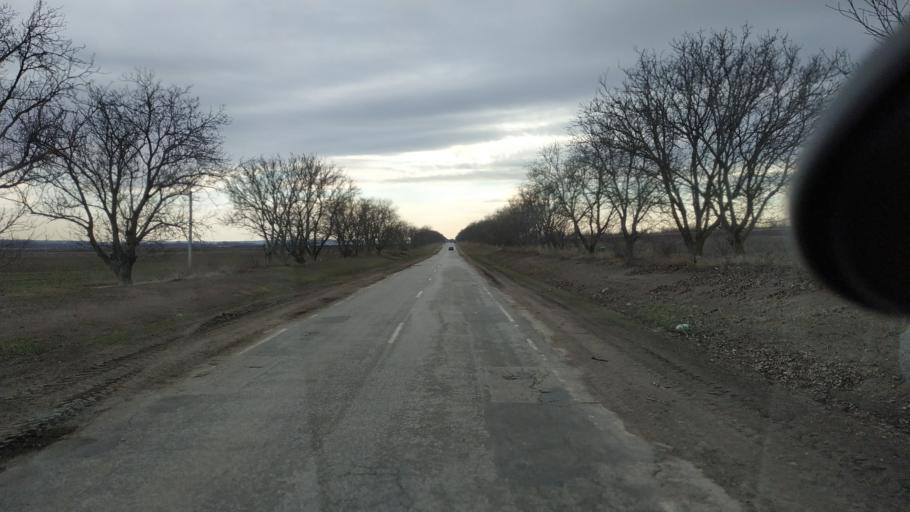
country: MD
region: Criuleni
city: Criuleni
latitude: 47.1879
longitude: 29.1433
